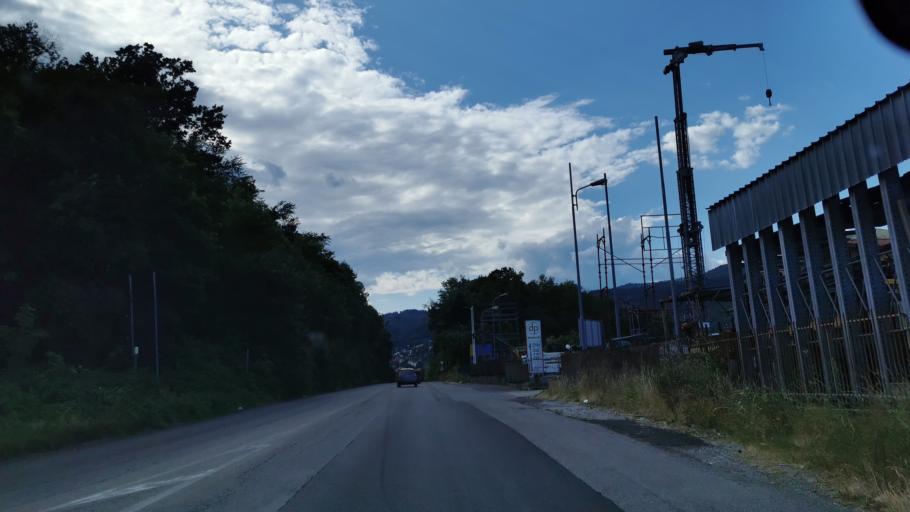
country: IT
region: Lombardy
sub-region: Provincia di Como
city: Albese Con Cassano
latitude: 45.7914
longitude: 9.1544
